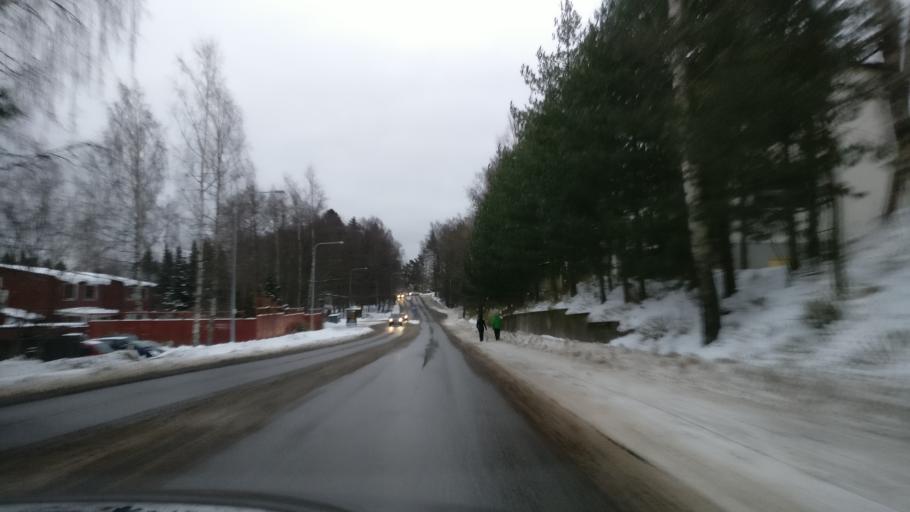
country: FI
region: Uusimaa
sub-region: Helsinki
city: Helsinki
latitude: 60.1668
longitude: 25.0523
